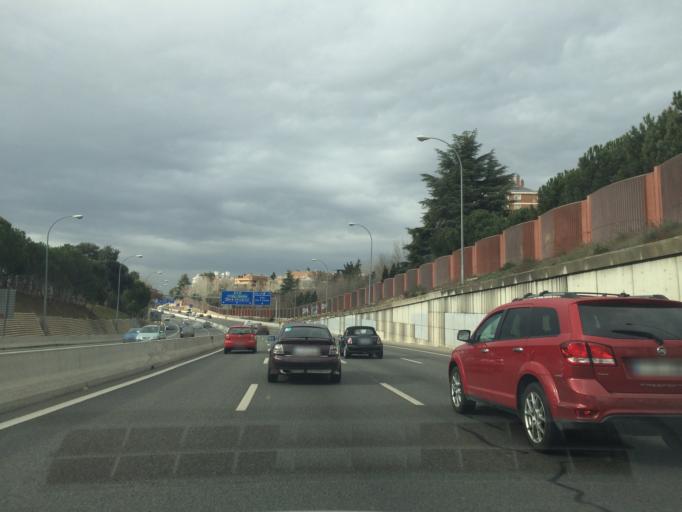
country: ES
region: Madrid
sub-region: Provincia de Madrid
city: Tetuan de las Victorias
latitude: 40.4742
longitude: -3.7398
